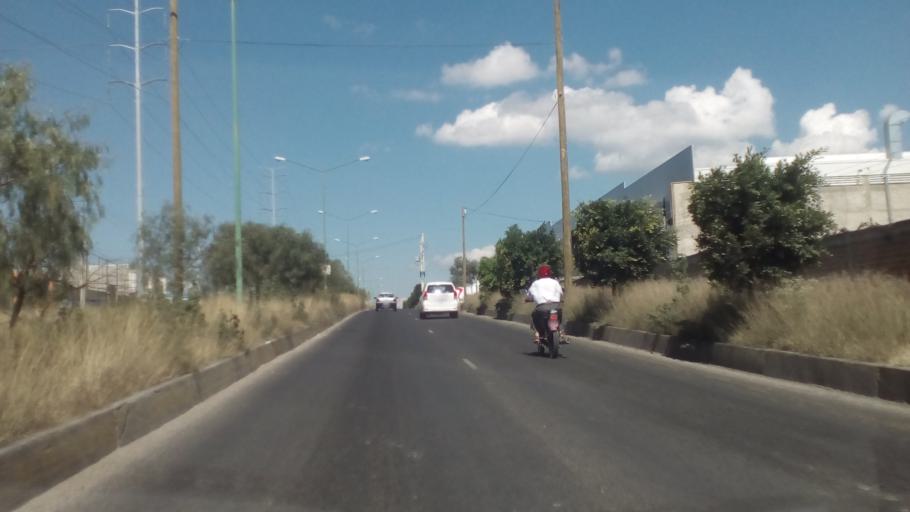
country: MX
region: Guanajuato
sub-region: Leon
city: La Ermita
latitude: 21.1540
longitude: -101.7302
